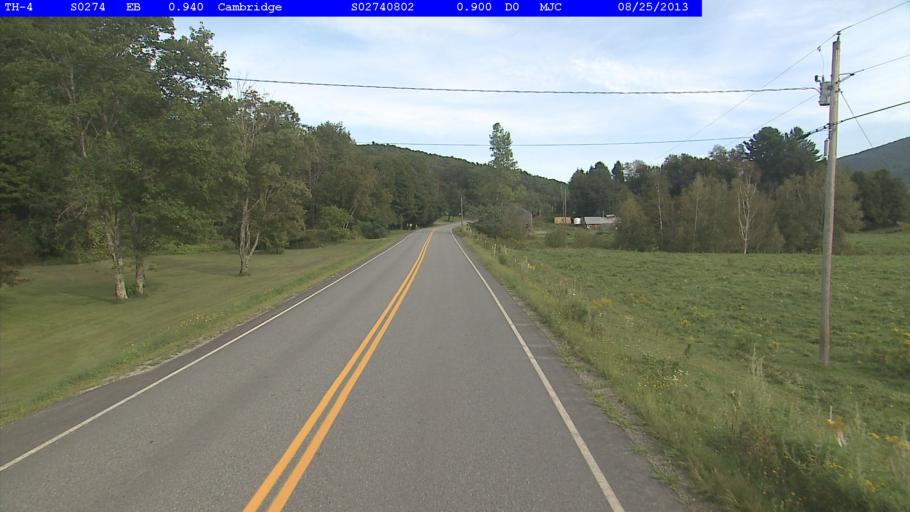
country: US
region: Vermont
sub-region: Lamoille County
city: Johnson
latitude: 44.6707
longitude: -72.7654
